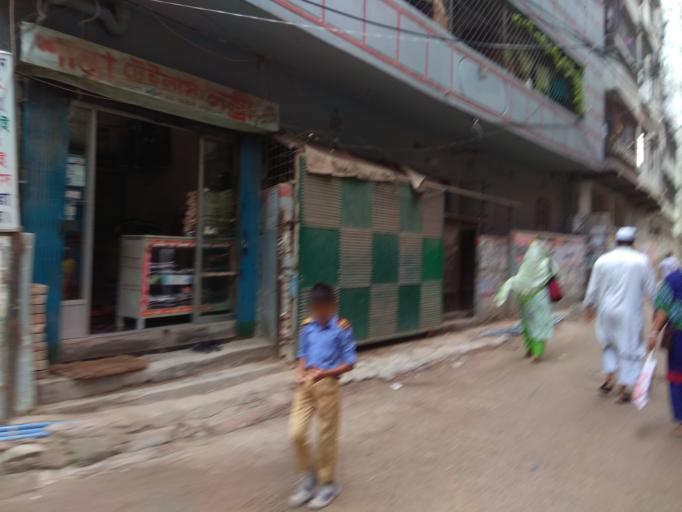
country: BD
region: Dhaka
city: Azimpur
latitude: 23.7929
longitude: 90.3724
